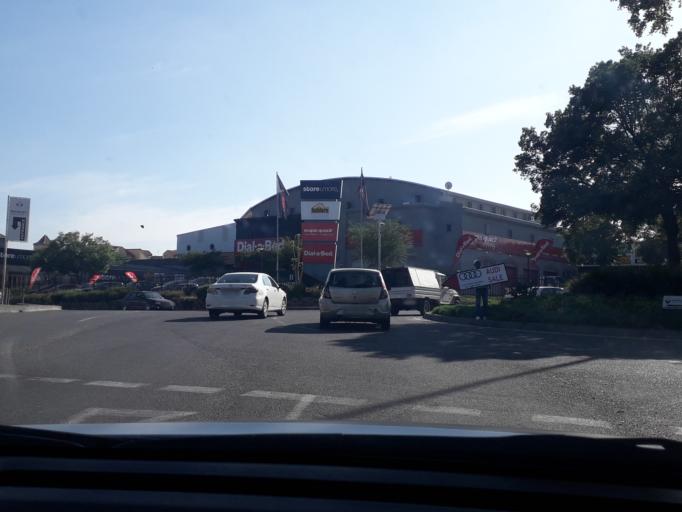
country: ZA
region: Gauteng
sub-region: City of Johannesburg Metropolitan Municipality
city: Diepsloot
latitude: -26.0159
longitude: 28.0115
